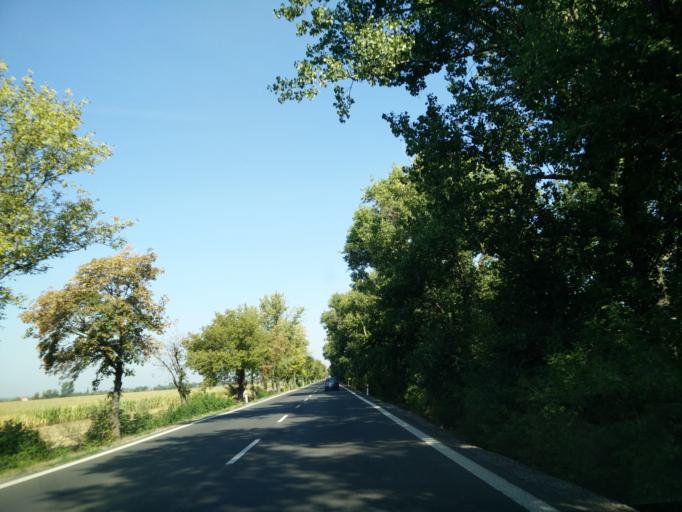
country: SK
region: Nitriansky
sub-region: Okres Nitra
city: Nitra
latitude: 48.3598
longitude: 18.0491
